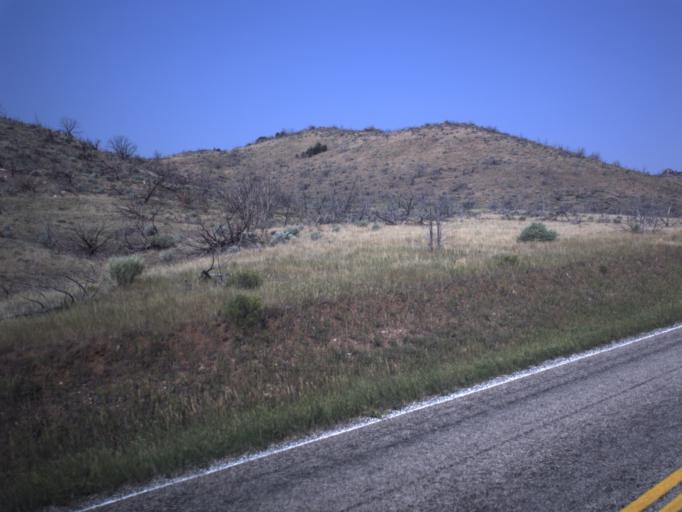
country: US
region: Utah
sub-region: Daggett County
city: Manila
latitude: 40.9478
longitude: -109.4412
